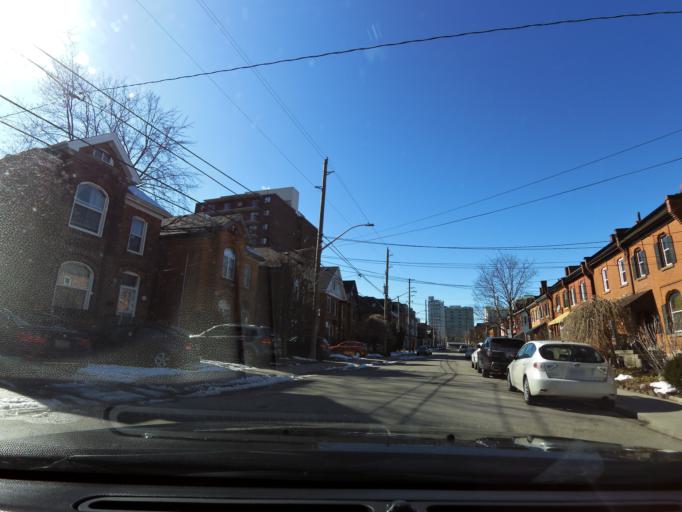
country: CA
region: Ontario
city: Hamilton
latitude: 43.2511
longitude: -79.8661
